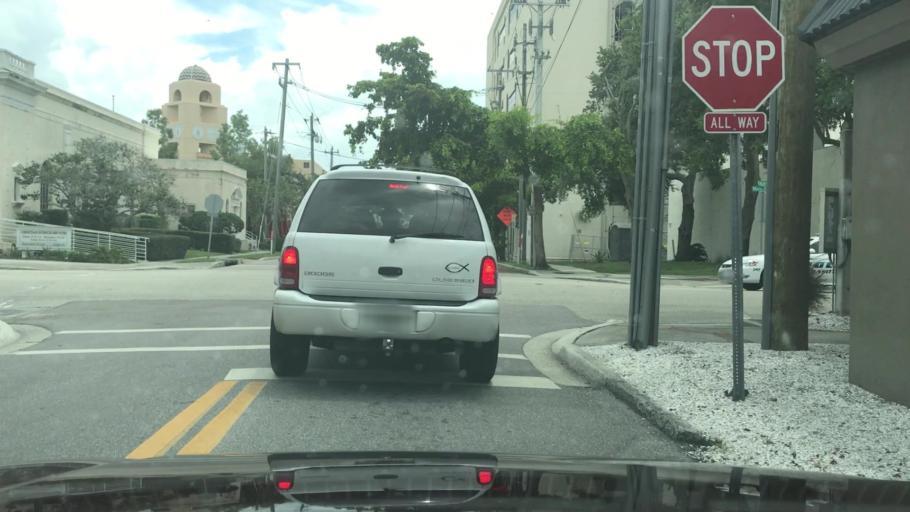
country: US
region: Florida
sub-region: Sarasota County
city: Sarasota
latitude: 27.3366
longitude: -82.5283
